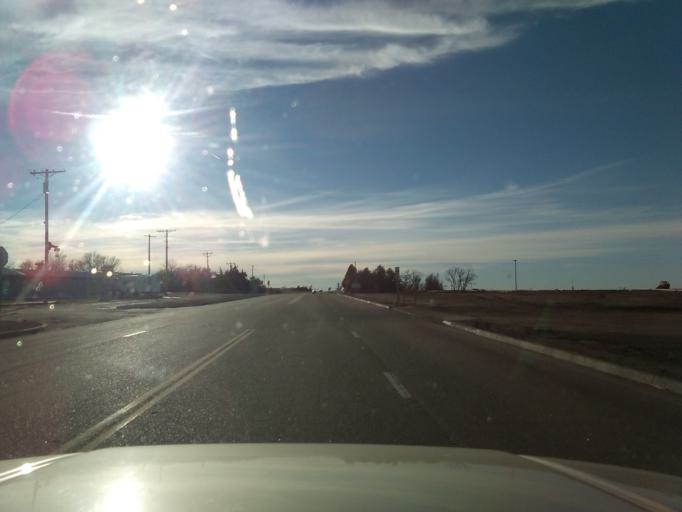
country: US
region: Kansas
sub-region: Sheridan County
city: Hoxie
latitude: 39.5436
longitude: -100.5689
